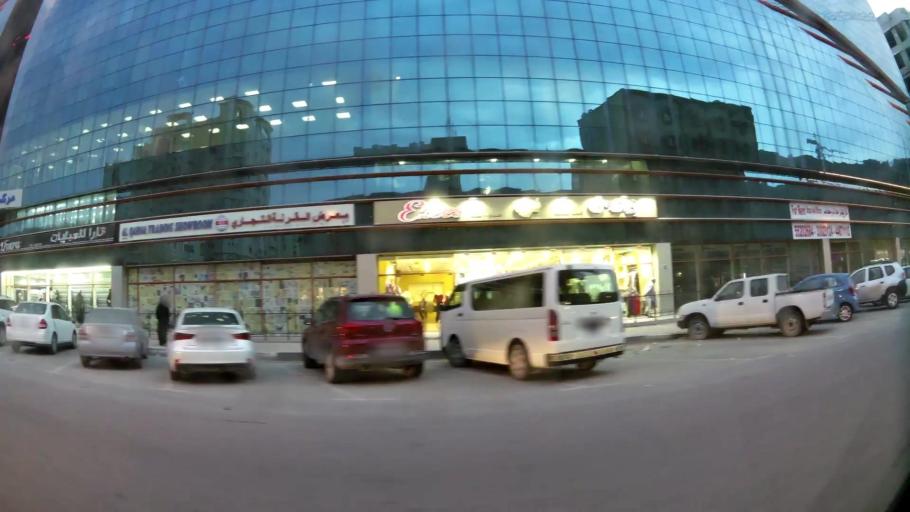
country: QA
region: Baladiyat ad Dawhah
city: Doha
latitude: 25.2723
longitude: 51.5254
